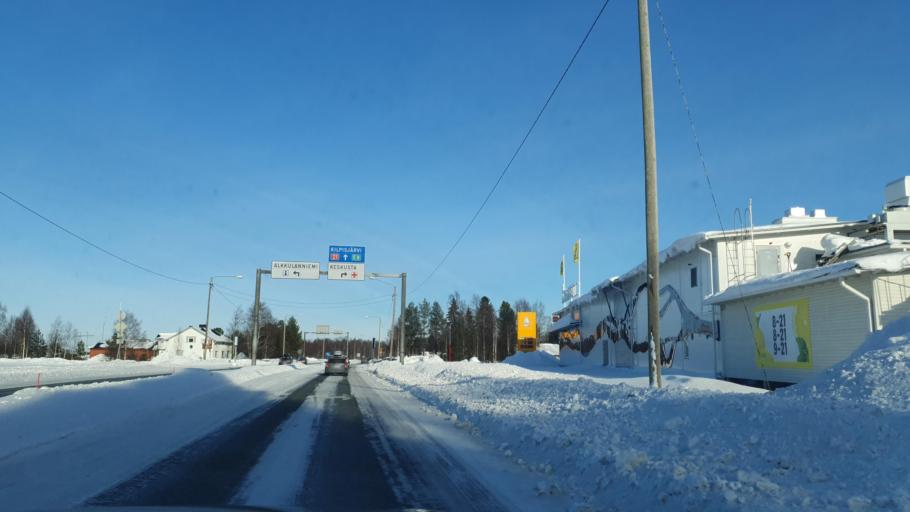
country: FI
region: Lapland
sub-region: Torniolaakso
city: Ylitornio
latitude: 66.3218
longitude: 23.6680
